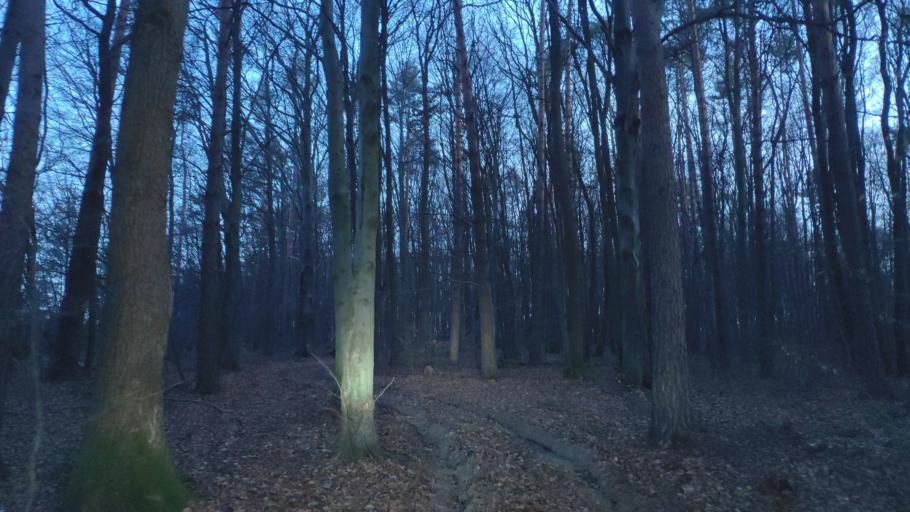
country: SK
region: Kosicky
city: Kosice
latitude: 48.8347
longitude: 21.2480
